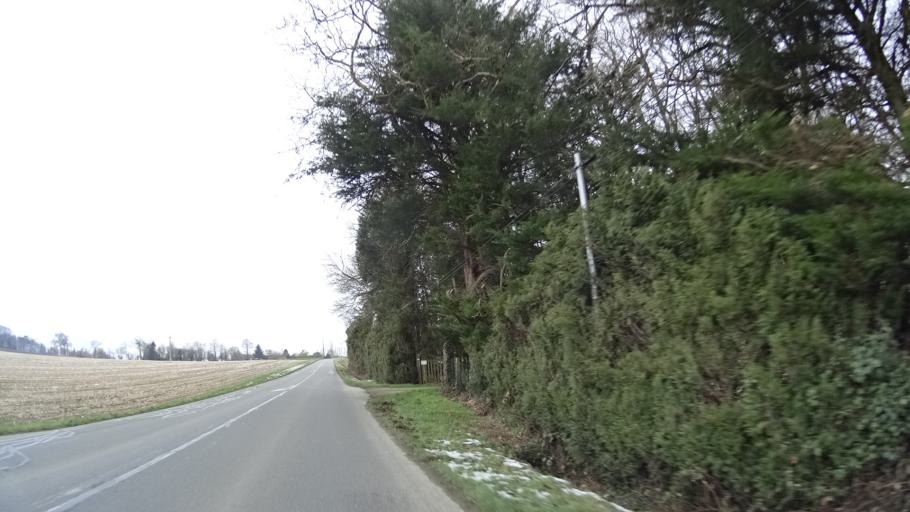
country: FR
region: Brittany
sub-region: Departement d'Ille-et-Vilaine
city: Irodouer
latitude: 48.2579
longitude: -1.9886
